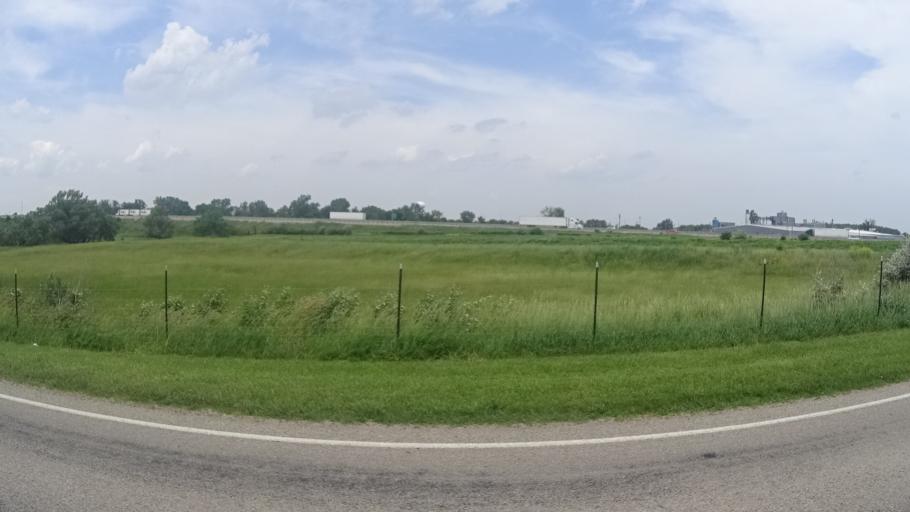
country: US
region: Ohio
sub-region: Erie County
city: Milan
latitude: 41.3225
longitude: -82.6261
